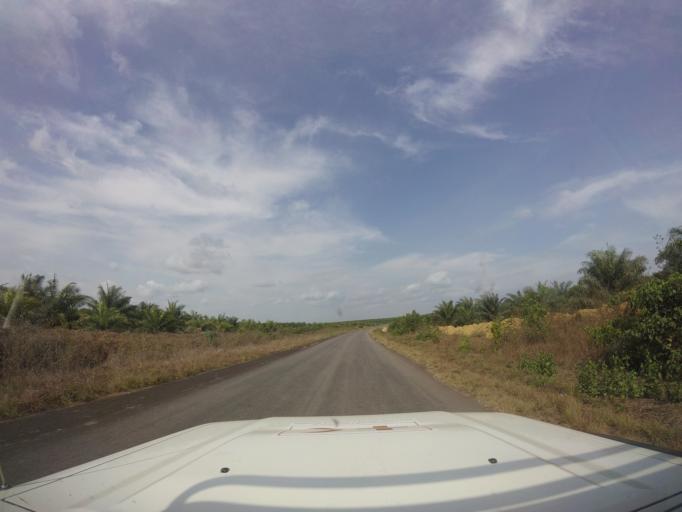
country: LR
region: Bomi
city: Tubmanburg
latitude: 6.7256
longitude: -11.0467
